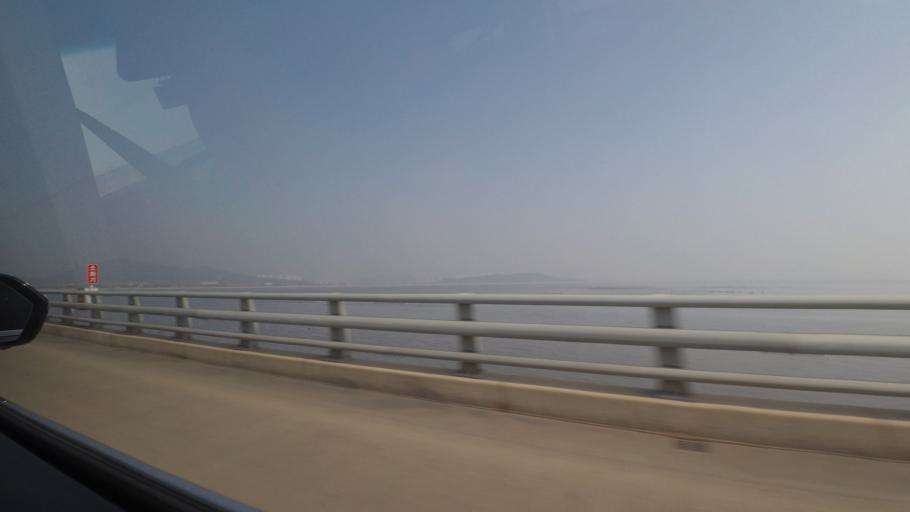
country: KR
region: Incheon
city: Incheon
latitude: 37.4533
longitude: 126.5261
